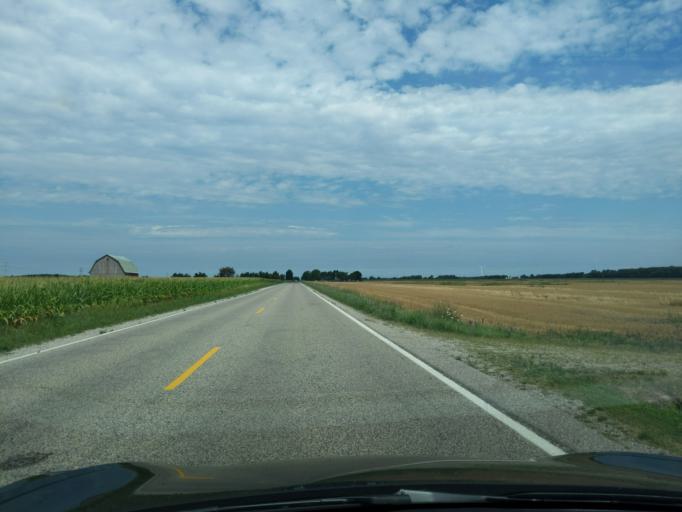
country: US
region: Michigan
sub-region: Gratiot County
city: Breckenridge
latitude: 43.3429
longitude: -84.4297
